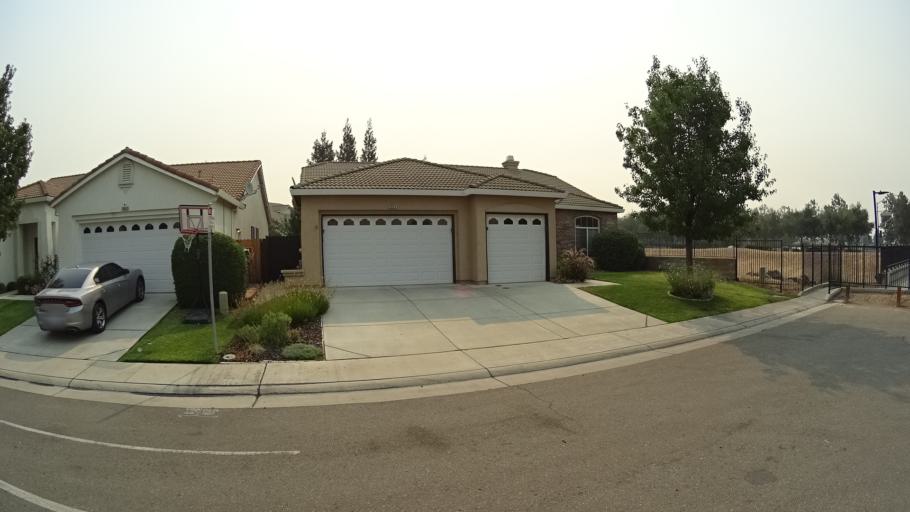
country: US
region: California
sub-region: Sacramento County
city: Laguna
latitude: 38.3948
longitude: -121.4320
